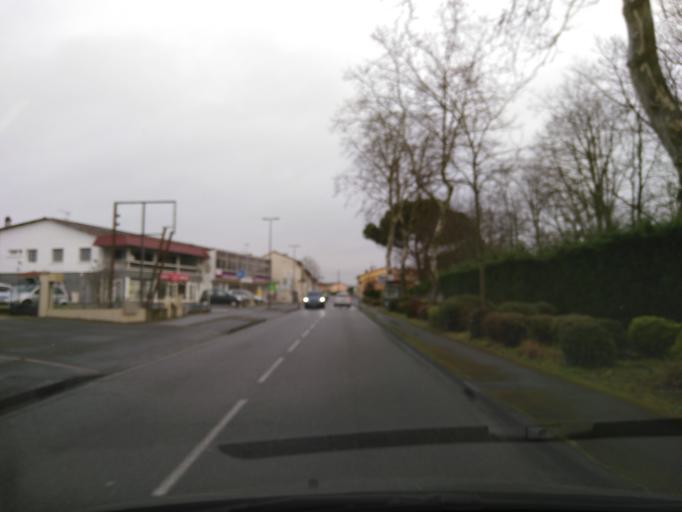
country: FR
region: Midi-Pyrenees
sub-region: Departement de la Haute-Garonne
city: Carbonne
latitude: 43.2959
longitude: 1.2174
